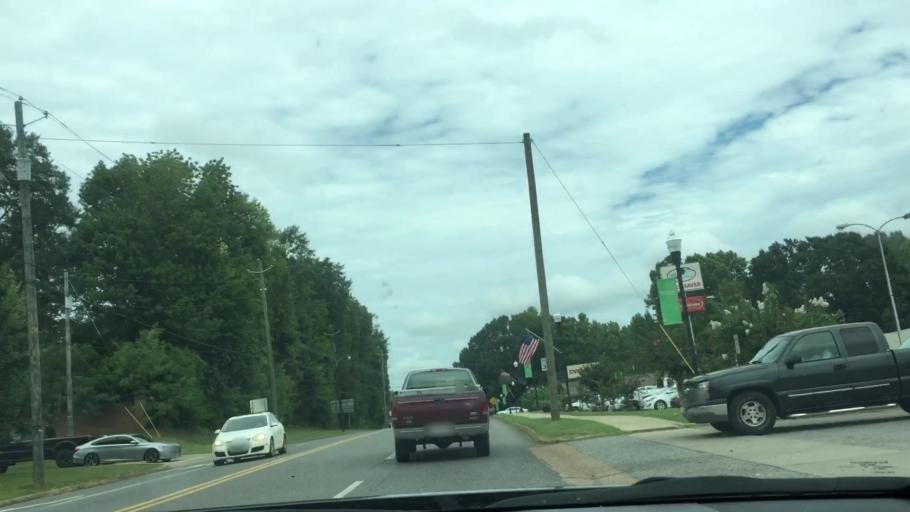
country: US
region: Alabama
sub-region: Hale County
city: Greensboro
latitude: 32.6997
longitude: -87.5953
